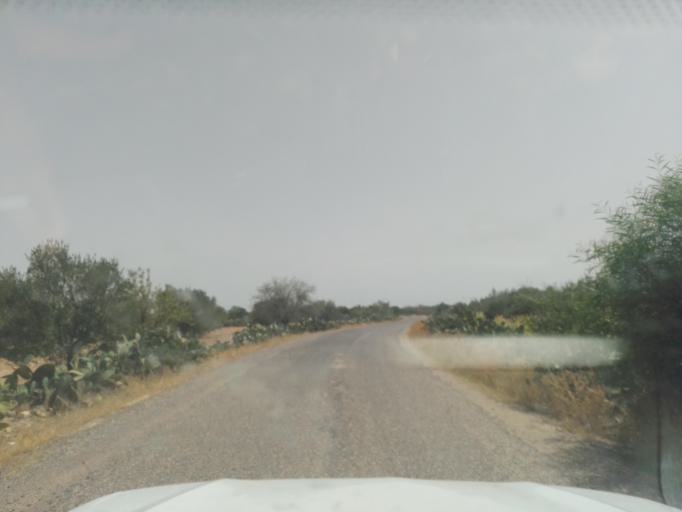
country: TN
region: Al Qasrayn
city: Kasserine
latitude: 35.2673
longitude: 9.0033
